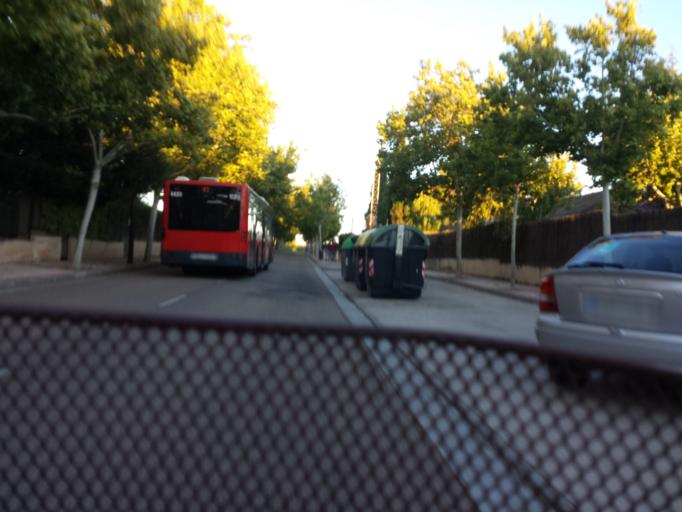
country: ES
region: Aragon
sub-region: Provincia de Zaragoza
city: Montecanal
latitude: 41.6291
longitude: -0.9448
